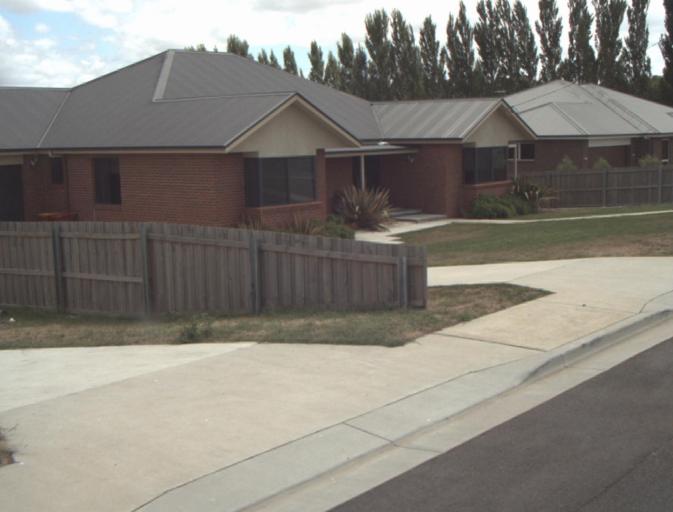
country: AU
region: Tasmania
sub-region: Launceston
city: Newstead
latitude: -41.4625
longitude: 147.2029
